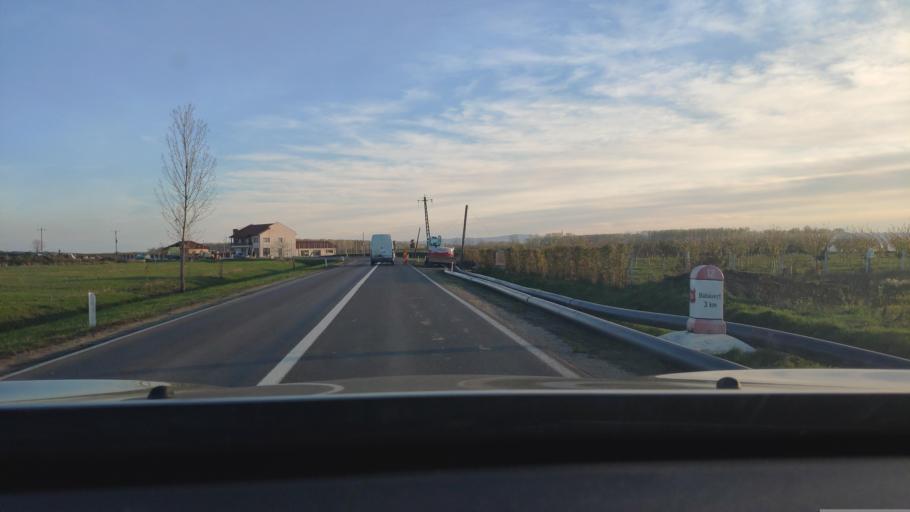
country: RO
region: Satu Mare
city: Culciu Mic
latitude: 47.7862
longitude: 23.0554
